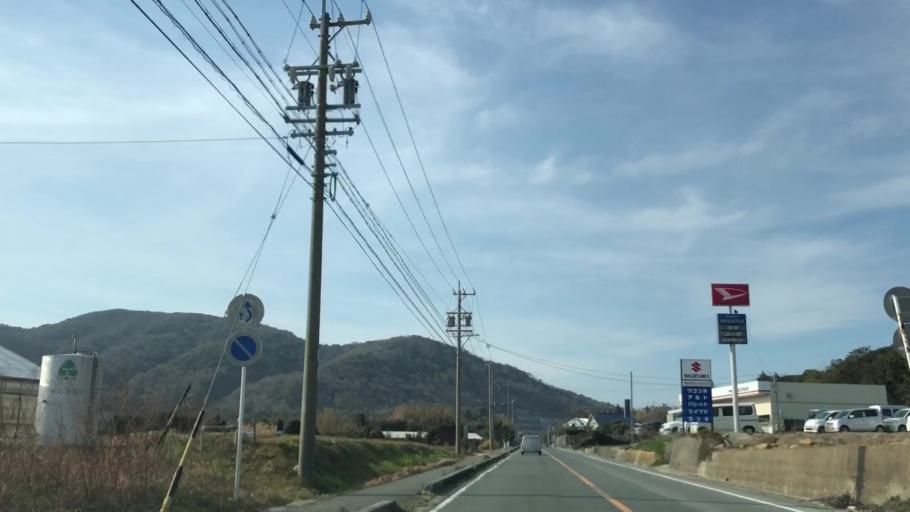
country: JP
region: Aichi
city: Tahara
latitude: 34.6771
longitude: 137.2533
